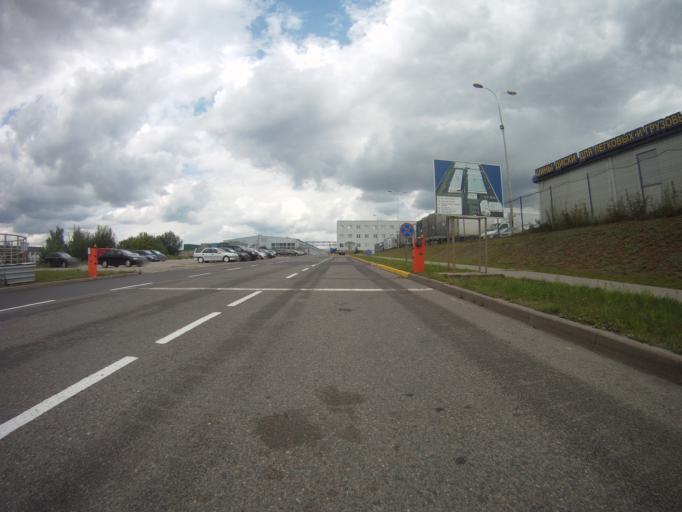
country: BY
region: Minsk
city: Malinovka
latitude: 53.8785
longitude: 27.4099
